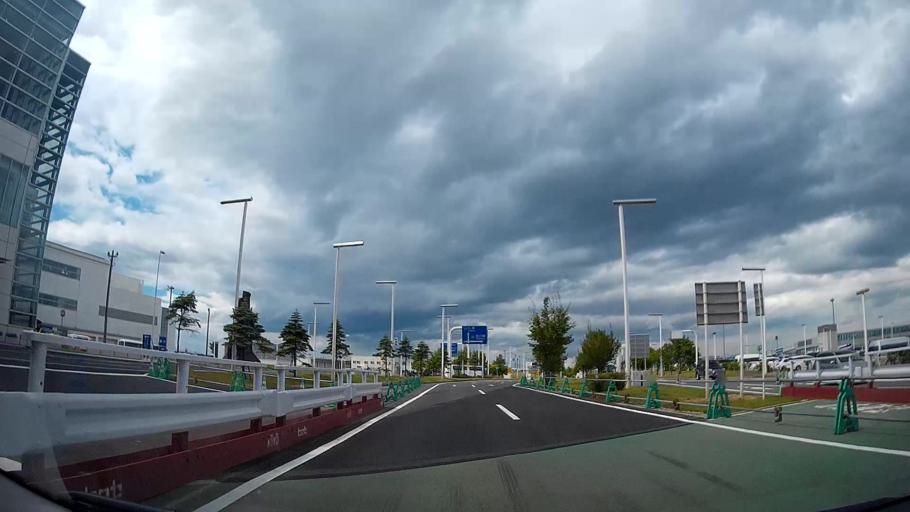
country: JP
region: Hokkaido
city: Chitose
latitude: 42.7875
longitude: 141.6768
